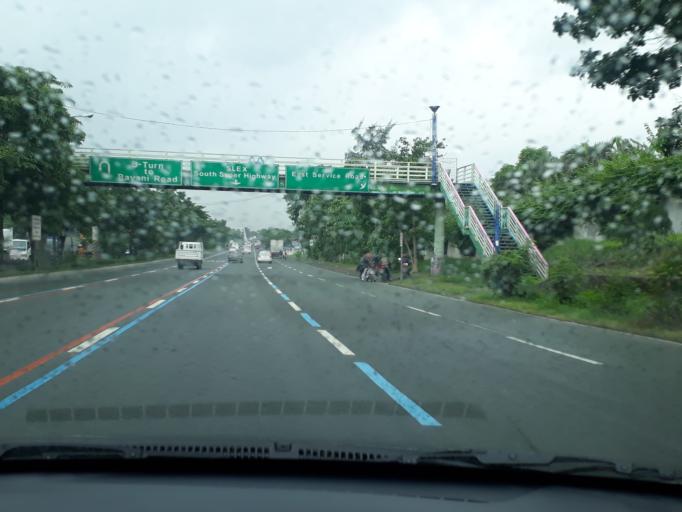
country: PH
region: Calabarzon
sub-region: Province of Rizal
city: Taguig
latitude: 14.5163
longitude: 121.0450
